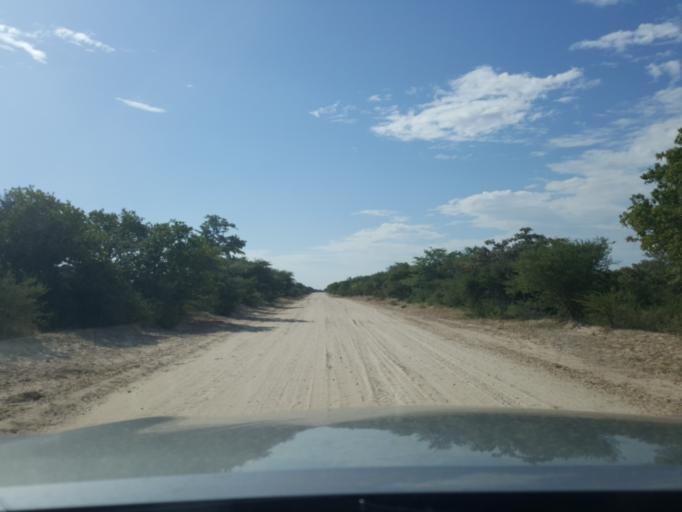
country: BW
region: Kweneng
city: Khudumelapye
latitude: -23.4912
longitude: 24.6994
